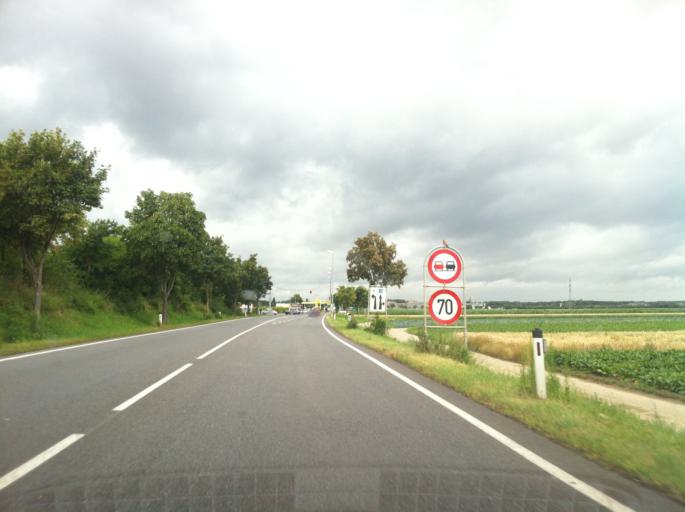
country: AT
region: Lower Austria
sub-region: Politischer Bezirk Tulln
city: Langenrohr
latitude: 48.3078
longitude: 16.0140
